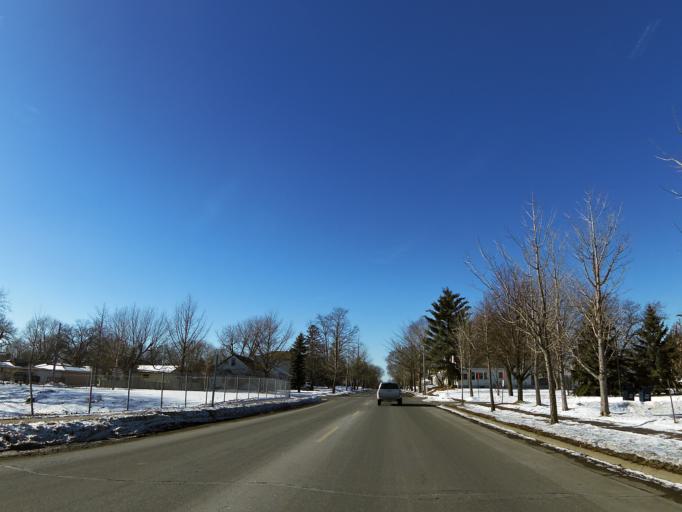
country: US
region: Minnesota
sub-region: Ramsey County
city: Maplewood
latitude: 44.9631
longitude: -93.0408
